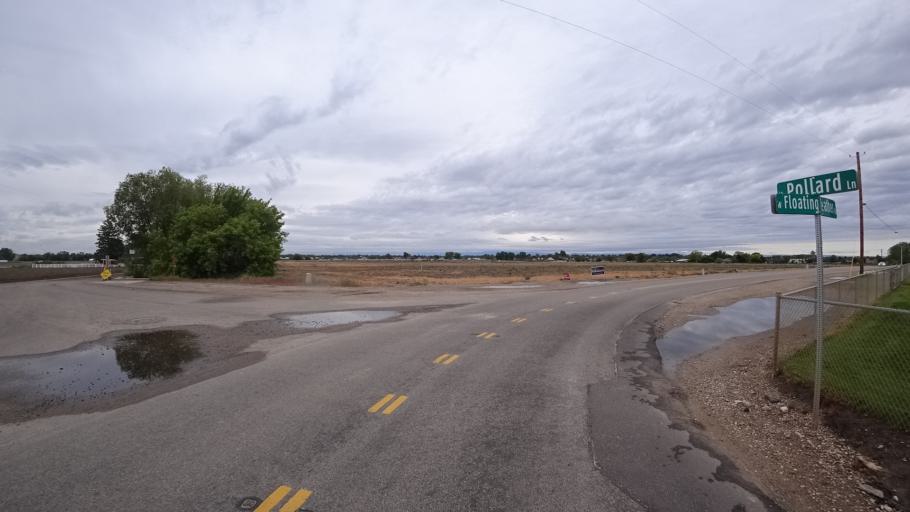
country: US
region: Idaho
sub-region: Ada County
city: Star
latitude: 43.7065
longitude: -116.4685
